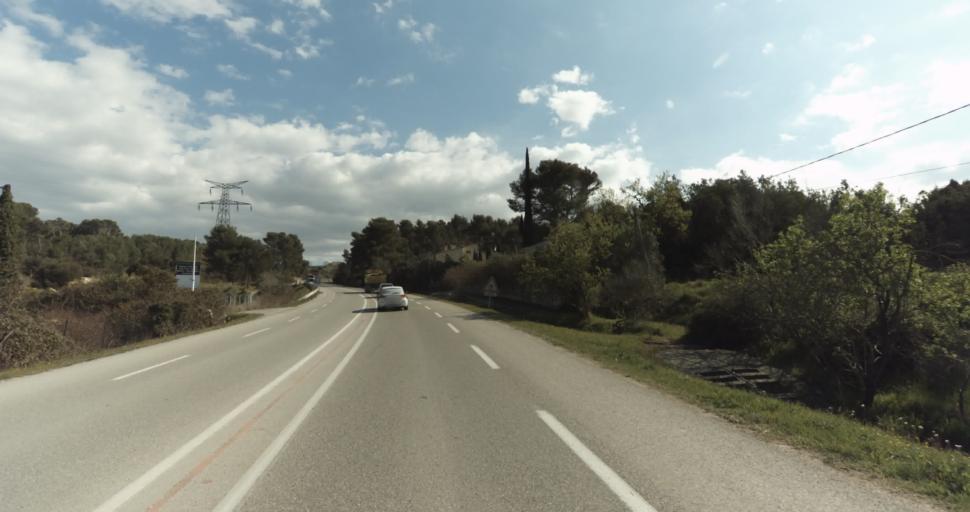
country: FR
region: Provence-Alpes-Cote d'Azur
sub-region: Departement des Bouches-du-Rhone
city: Gardanne
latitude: 43.4591
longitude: 5.4896
